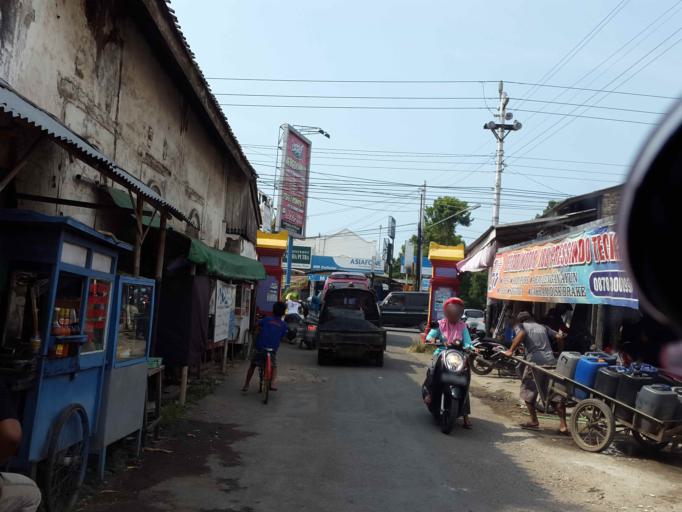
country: ID
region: Central Java
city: Pemalang
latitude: -6.8912
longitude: 109.3929
